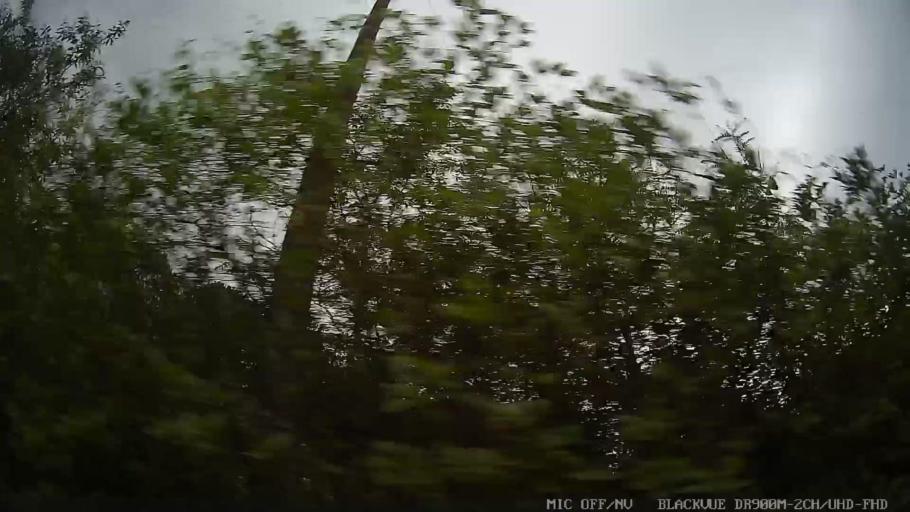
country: BR
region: Sao Paulo
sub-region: Itatiba
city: Itatiba
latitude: -23.0382
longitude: -46.8940
